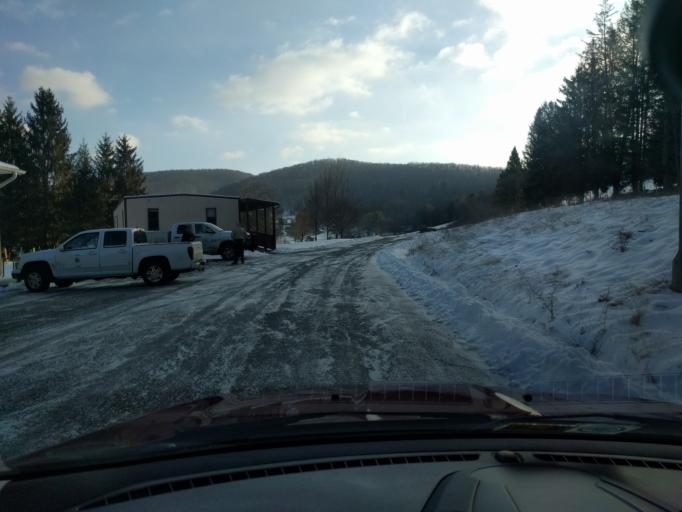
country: US
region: West Virginia
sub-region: Pocahontas County
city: Marlinton
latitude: 38.2151
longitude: -80.0804
